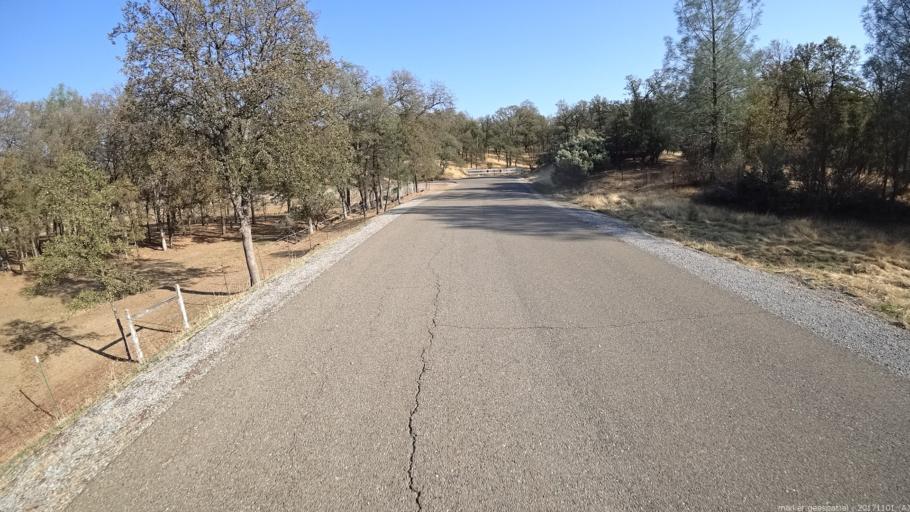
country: US
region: California
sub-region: Shasta County
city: Bella Vista
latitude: 40.6719
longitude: -122.2916
